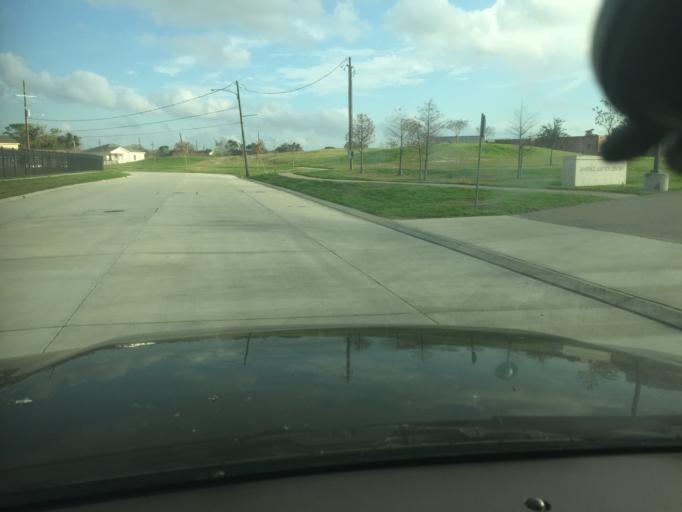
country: US
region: Louisiana
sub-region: Orleans Parish
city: New Orleans
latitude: 29.9959
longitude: -90.0843
